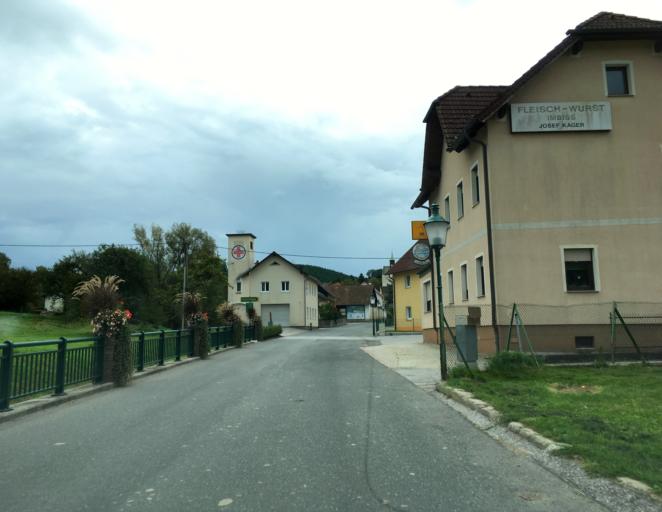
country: AT
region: Lower Austria
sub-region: Politischer Bezirk Wiener Neustadt
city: Bad Schonau
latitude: 47.4978
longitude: 16.2336
